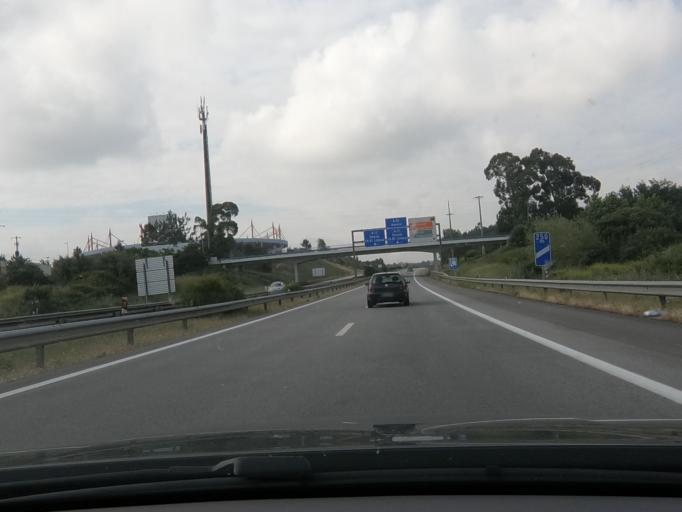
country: PT
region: Aveiro
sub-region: Aveiro
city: Eixo
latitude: 40.6537
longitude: -8.5939
